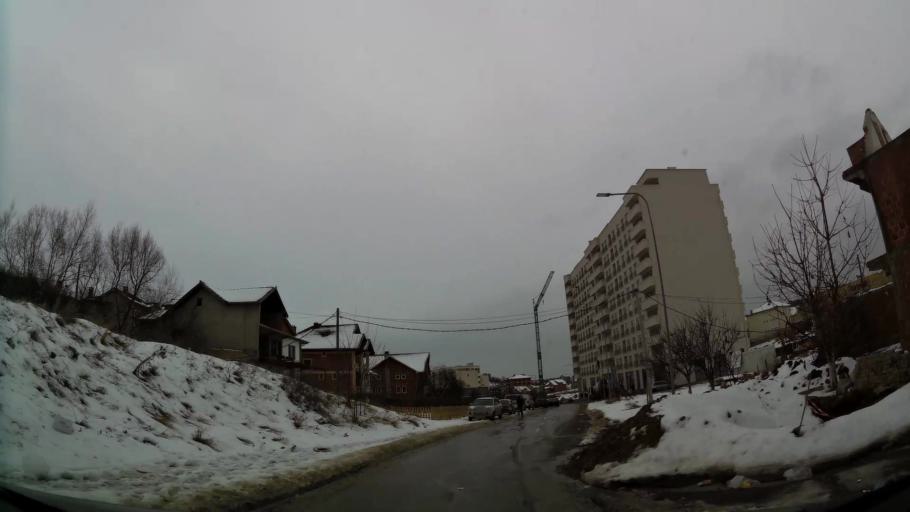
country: XK
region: Pristina
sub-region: Komuna e Prishtines
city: Pristina
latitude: 42.6455
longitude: 21.1839
